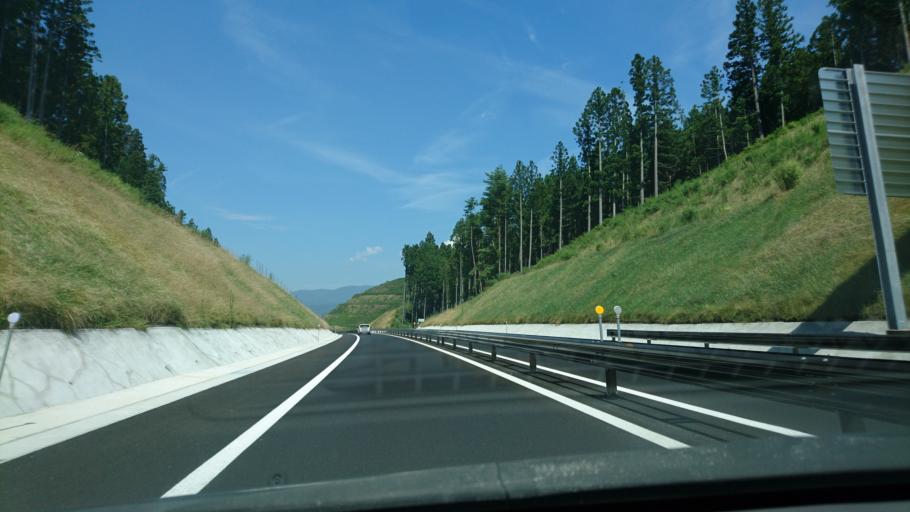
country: JP
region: Iwate
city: Ofunato
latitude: 38.9958
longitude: 141.6145
